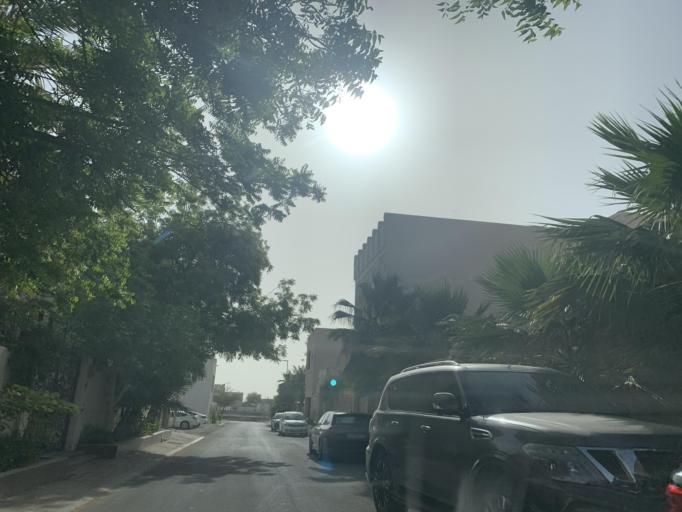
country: BH
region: Northern
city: Ar Rifa'
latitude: 26.1421
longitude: 50.5846
